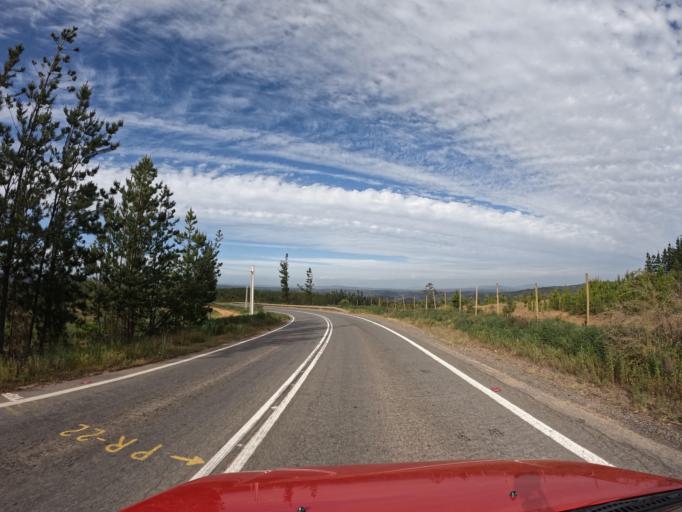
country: CL
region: O'Higgins
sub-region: Provincia de Colchagua
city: Santa Cruz
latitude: -34.3074
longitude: -71.8363
